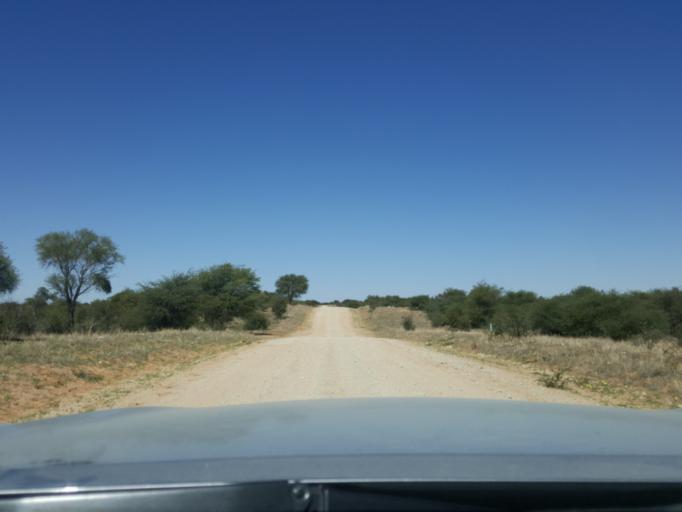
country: BW
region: Kgalagadi
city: Hukuntsi
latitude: -24.1052
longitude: 21.2321
